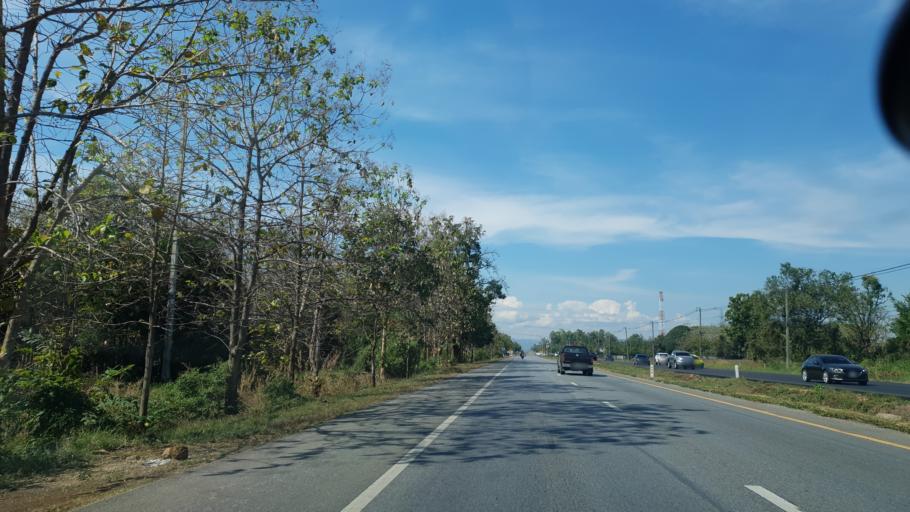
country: TH
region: Uttaradit
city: Tron
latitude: 17.5419
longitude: 100.1949
